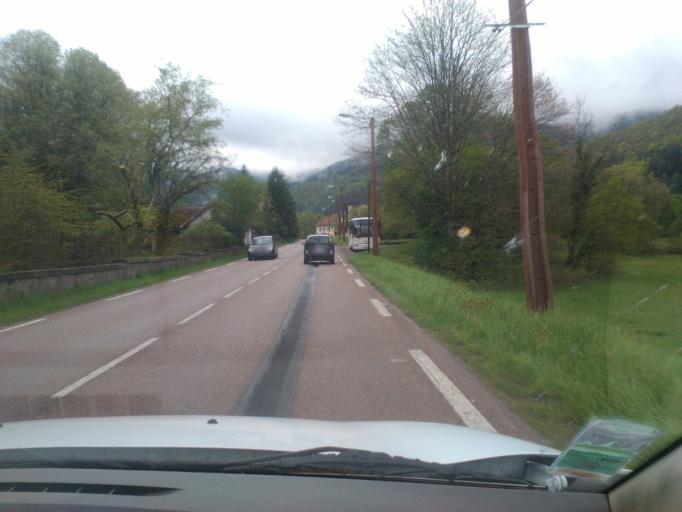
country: FR
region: Lorraine
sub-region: Departement des Vosges
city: Saulxures-sur-Moselotte
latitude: 47.9638
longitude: 6.7361
